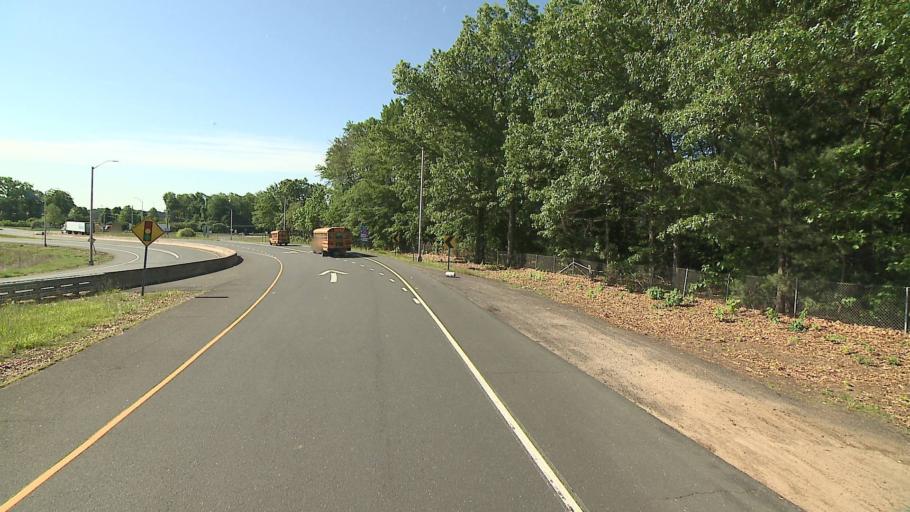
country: US
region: Connecticut
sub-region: Hartford County
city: South Windsor
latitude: 41.8049
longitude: -72.6174
